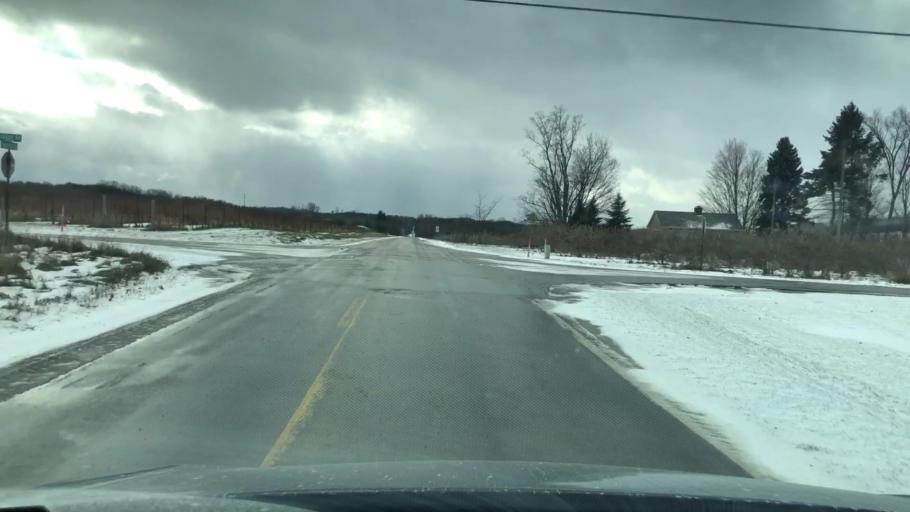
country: US
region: Michigan
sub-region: Antrim County
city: Elk Rapids
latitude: 44.9211
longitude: -85.5156
